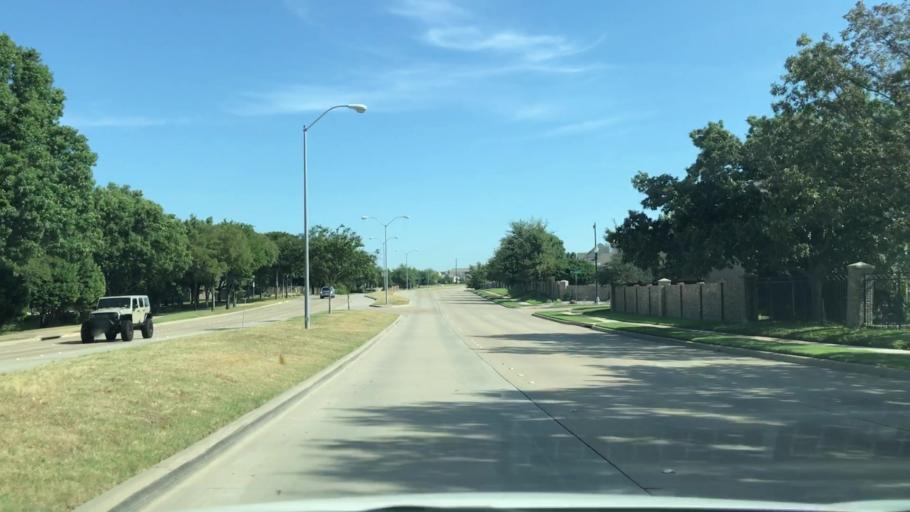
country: US
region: Texas
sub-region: Denton County
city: The Colony
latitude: 33.0626
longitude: -96.8394
